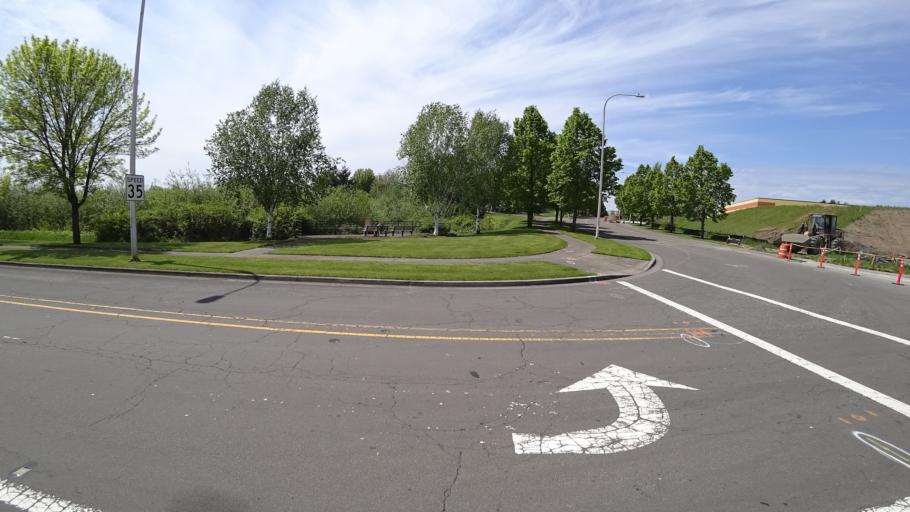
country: US
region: Oregon
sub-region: Washington County
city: Rockcreek
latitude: 45.5693
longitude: -122.9061
